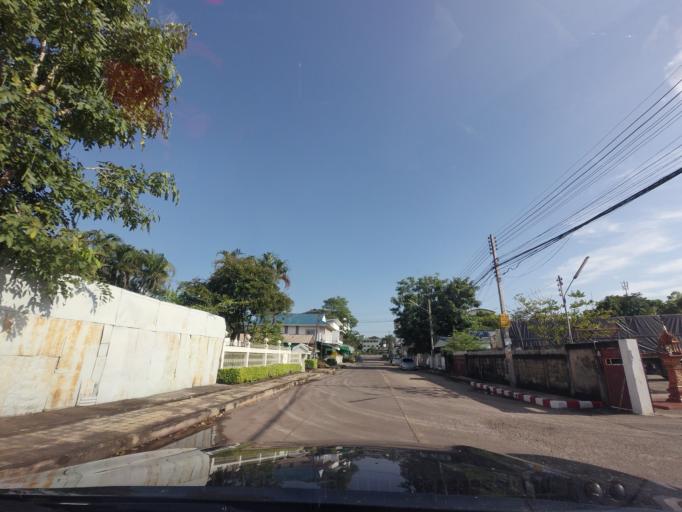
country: TH
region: Nong Khai
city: Nong Khai
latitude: 17.8815
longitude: 102.7502
